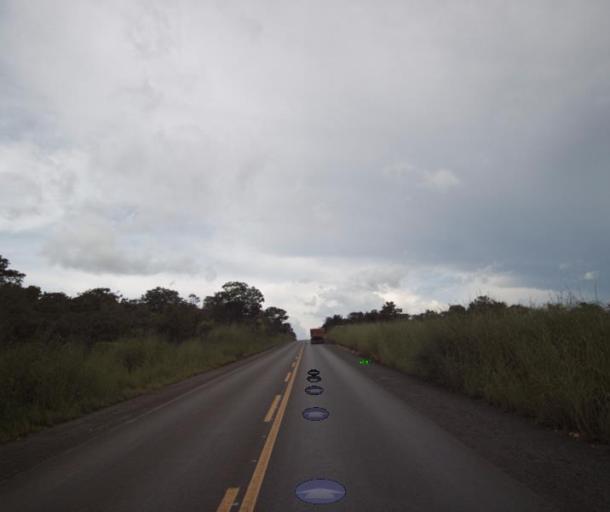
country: BR
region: Goias
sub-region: Niquelandia
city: Niquelandia
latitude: -14.4996
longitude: -48.5005
